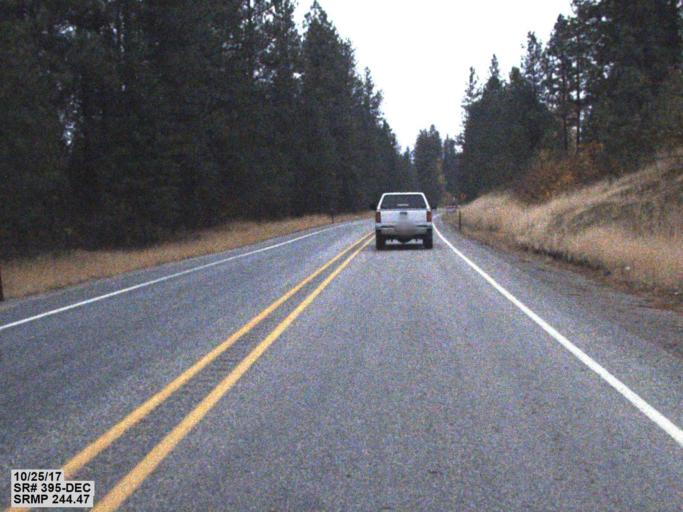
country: US
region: Washington
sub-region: Stevens County
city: Kettle Falls
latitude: 48.6627
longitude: -118.1138
